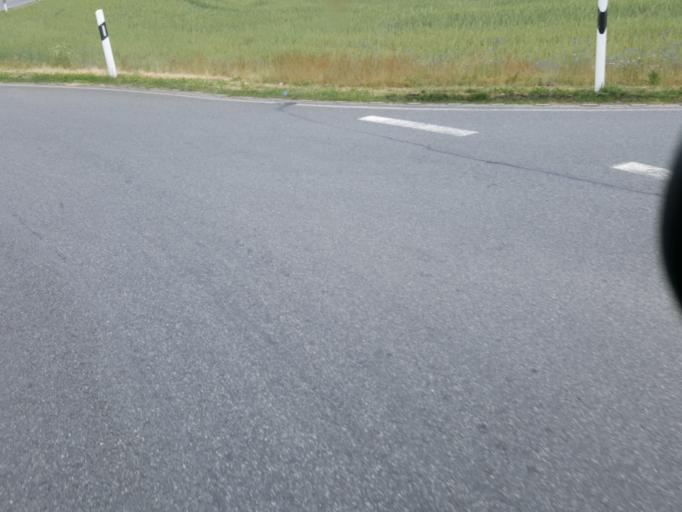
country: DE
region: Lower Saxony
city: Leese
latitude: 52.4913
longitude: 9.1237
